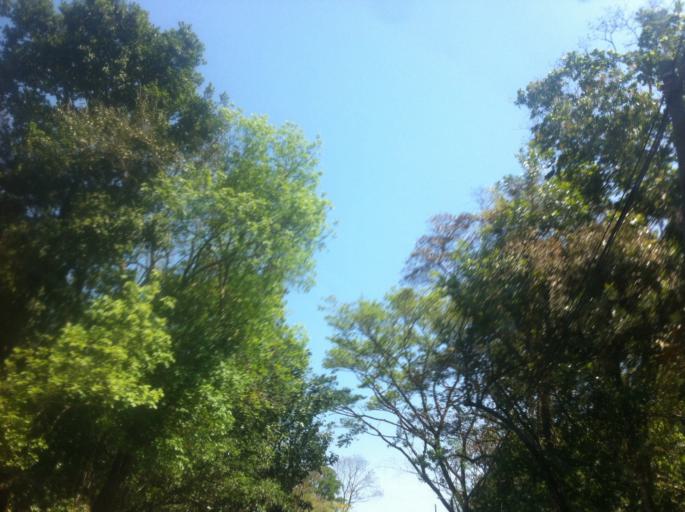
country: CR
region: Guanacaste
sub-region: Canton de Nicoya
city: Nicoya
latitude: 10.0983
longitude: -85.4598
